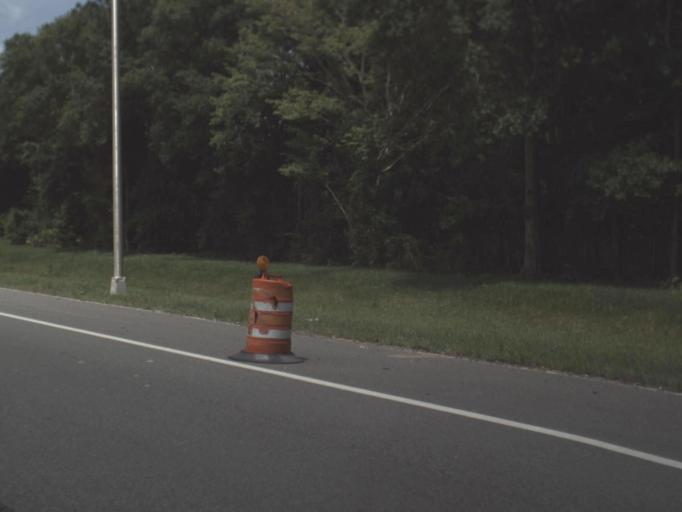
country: US
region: Florida
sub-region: Clay County
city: Bellair-Meadowbrook Terrace
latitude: 30.2160
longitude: -81.7608
